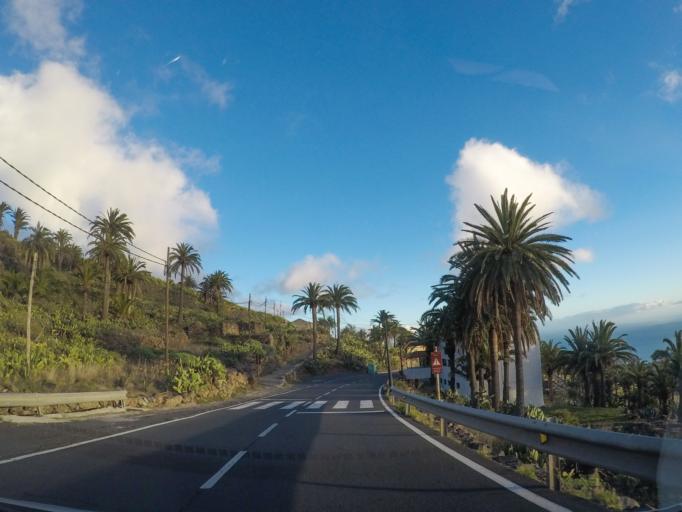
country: ES
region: Canary Islands
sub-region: Provincia de Santa Cruz de Tenerife
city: Alajero
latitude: 28.0603
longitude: -17.2357
